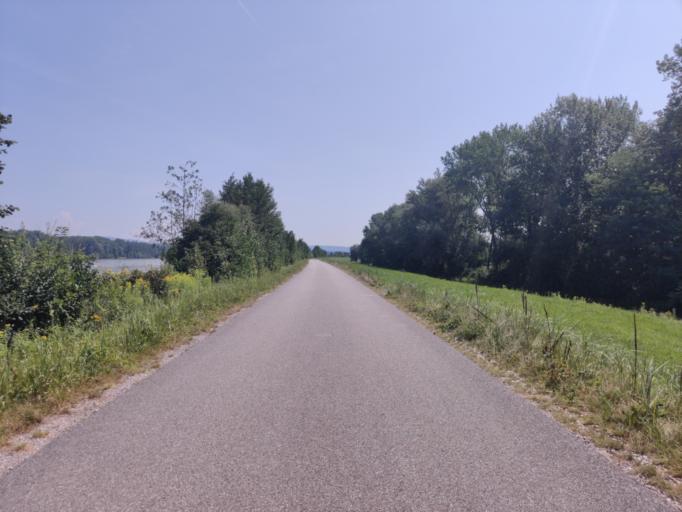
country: AT
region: Upper Austria
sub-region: Politischer Bezirk Urfahr-Umgebung
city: Goldworth
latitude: 48.3162
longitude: 14.0745
